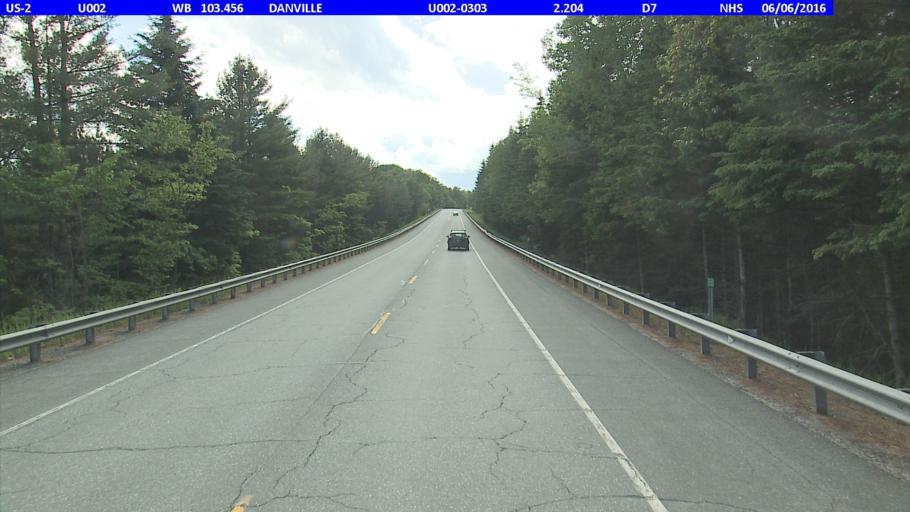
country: US
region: Vermont
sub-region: Caledonia County
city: Saint Johnsbury
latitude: 44.4087
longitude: -72.1852
